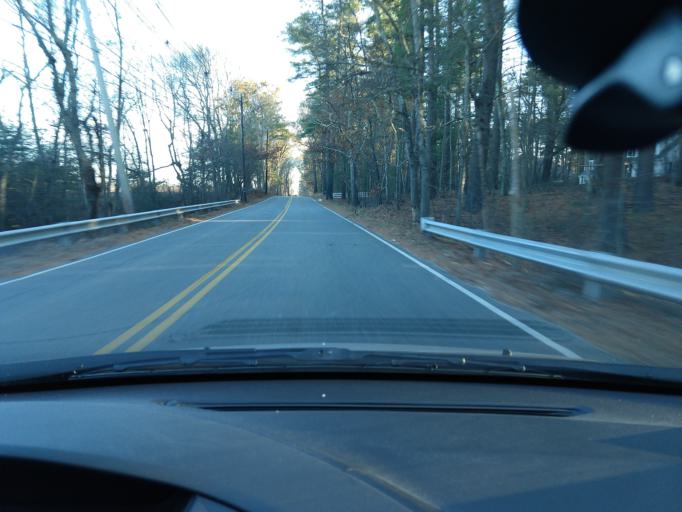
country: US
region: Massachusetts
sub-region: Middlesex County
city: Carlisle
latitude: 42.5127
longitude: -71.3187
